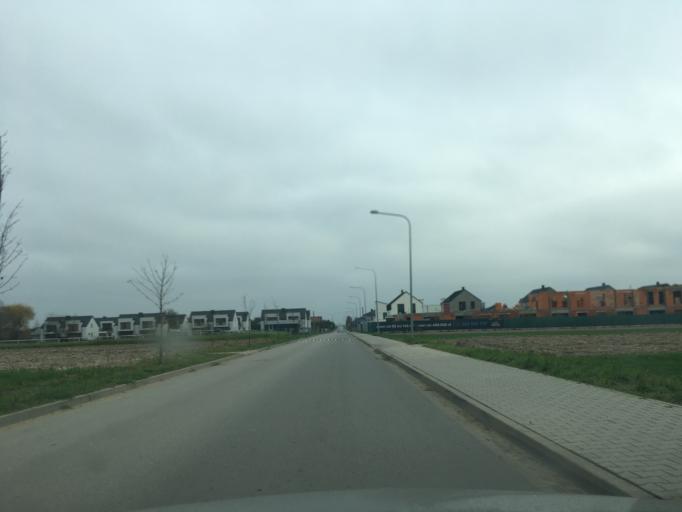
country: PL
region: Masovian Voivodeship
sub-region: Powiat piaseczynski
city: Lesznowola
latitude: 52.0849
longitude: 20.9412
